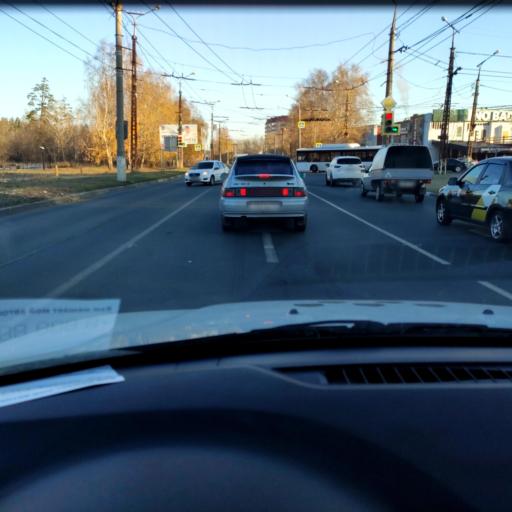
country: RU
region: Samara
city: Tol'yatti
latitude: 53.4985
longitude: 49.3886
